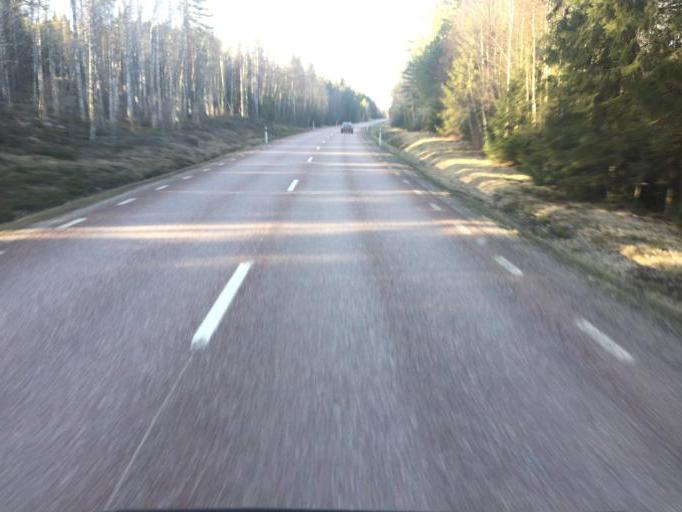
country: SE
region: Dalarna
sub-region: Gagnefs Kommun
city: Mockfjard
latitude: 60.4755
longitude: 14.7712
